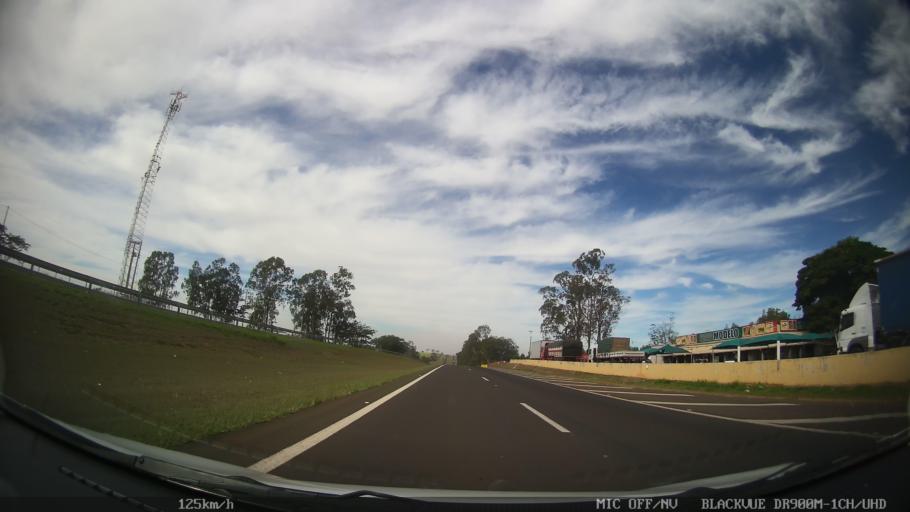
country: BR
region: Sao Paulo
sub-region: Taquaritinga
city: Taquaritinga
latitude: -21.5358
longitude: -48.5114
